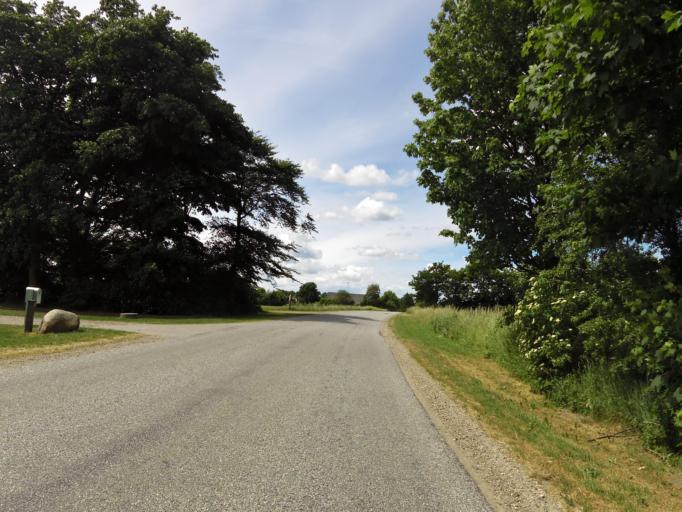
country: DK
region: South Denmark
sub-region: Esbjerg Kommune
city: Ribe
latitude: 55.2616
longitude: 8.8867
